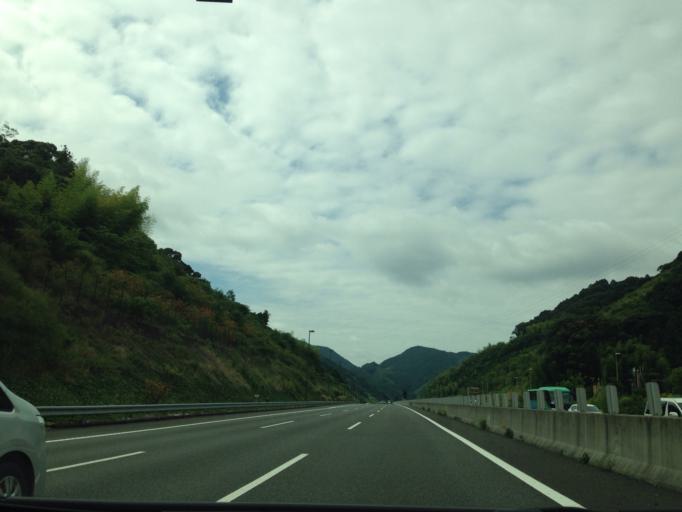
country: JP
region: Shizuoka
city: Shizuoka-shi
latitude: 34.9802
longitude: 138.2946
